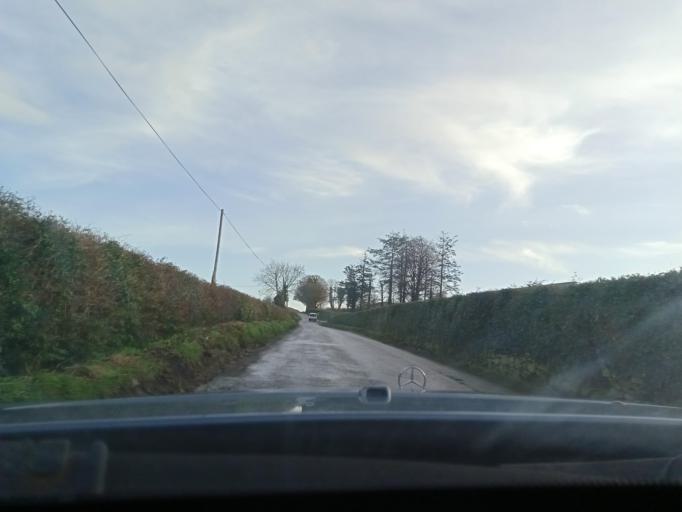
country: IE
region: Leinster
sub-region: Kilkenny
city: Callan
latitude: 52.4763
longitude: -7.4400
